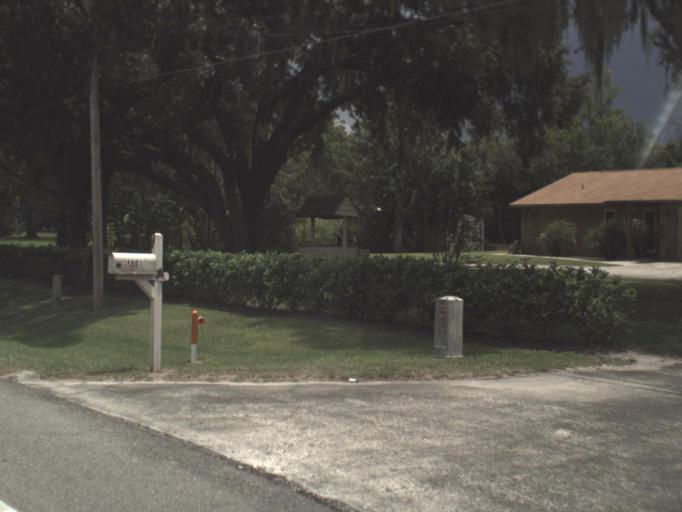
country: US
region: Florida
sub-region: Hillsborough County
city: Dover
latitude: 28.0213
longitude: -82.1953
